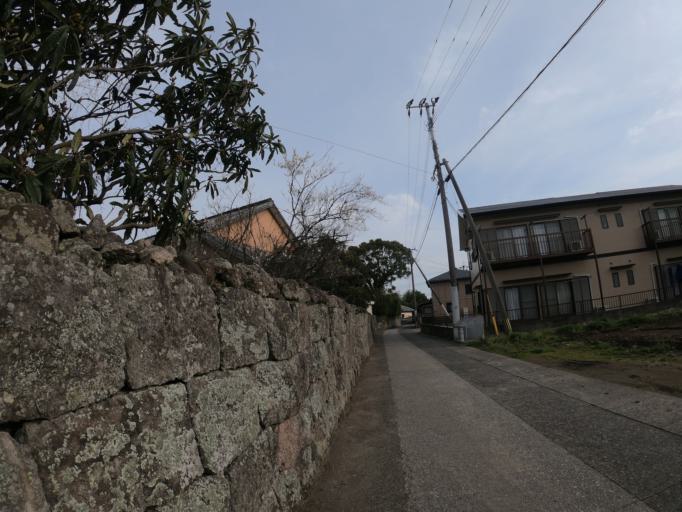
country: JP
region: Nagasaki
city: Shimabara
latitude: 32.6694
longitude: 130.3063
